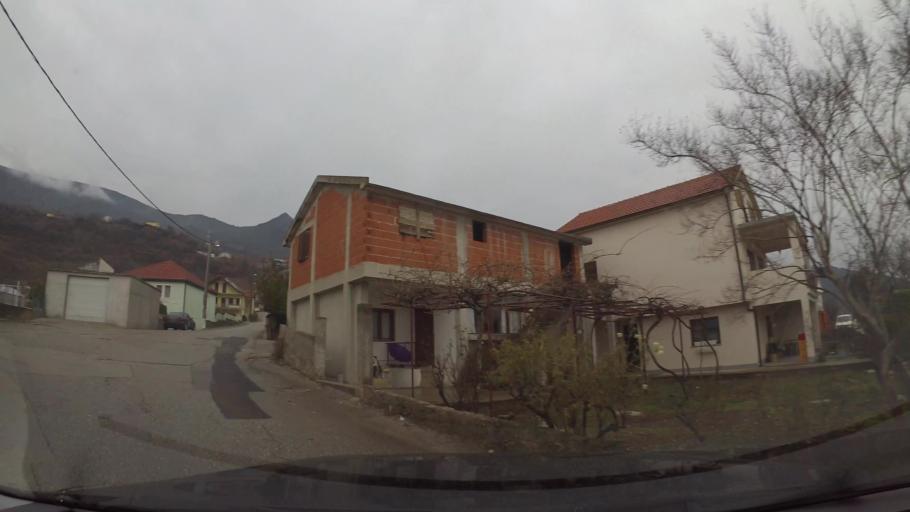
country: BA
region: Federation of Bosnia and Herzegovina
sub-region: Hercegovacko-Bosanski Kanton
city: Mostar
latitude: 43.3617
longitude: 17.8032
